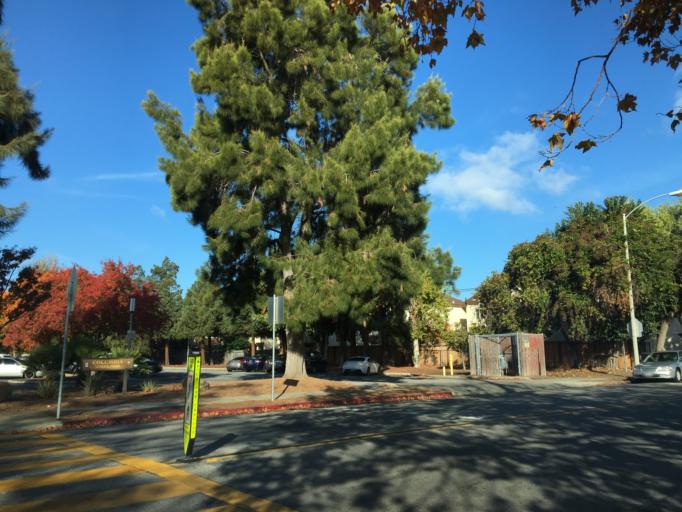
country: US
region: California
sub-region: Santa Clara County
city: Sunnyvale
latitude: 37.3950
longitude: -122.0182
